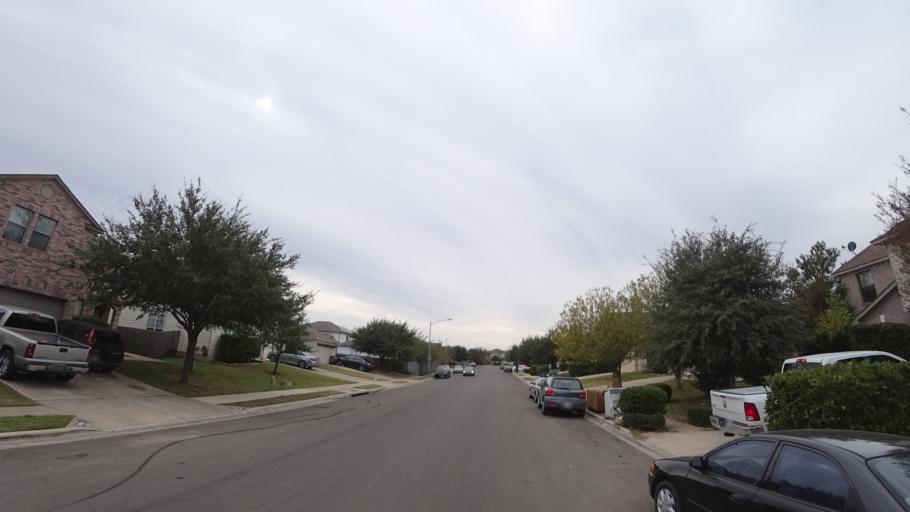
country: US
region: Texas
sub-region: Travis County
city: Onion Creek
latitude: 30.1594
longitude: -97.7412
